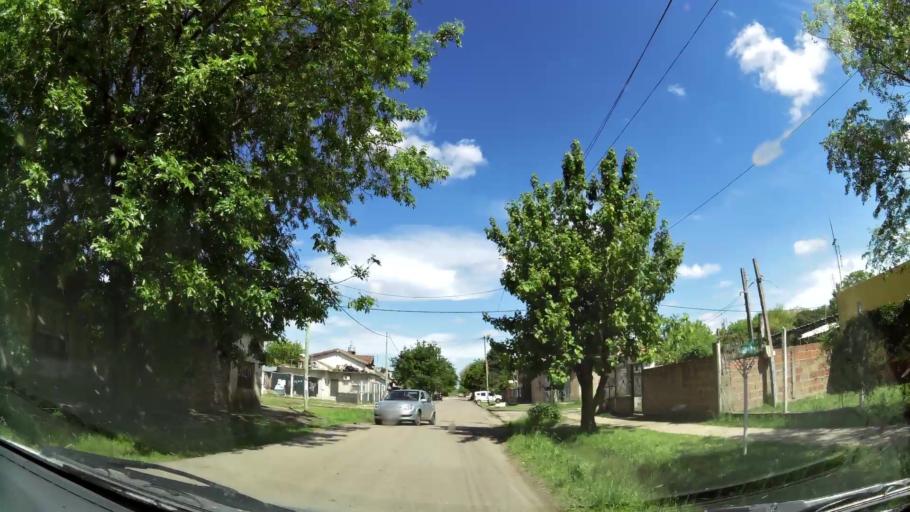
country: AR
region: Buenos Aires
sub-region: Partido de Quilmes
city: Quilmes
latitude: -34.8204
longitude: -58.2573
